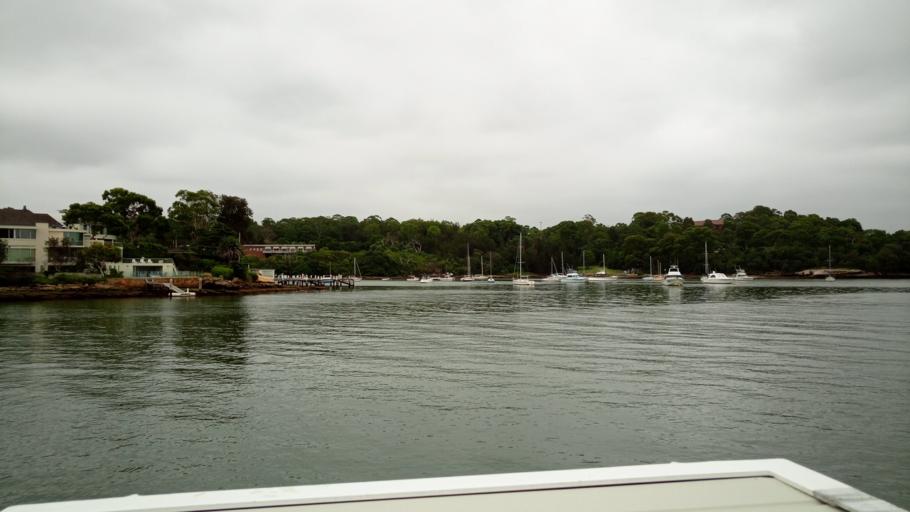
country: AU
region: New South Wales
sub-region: Canada Bay
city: Canada Bay
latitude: -33.8455
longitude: 151.1392
